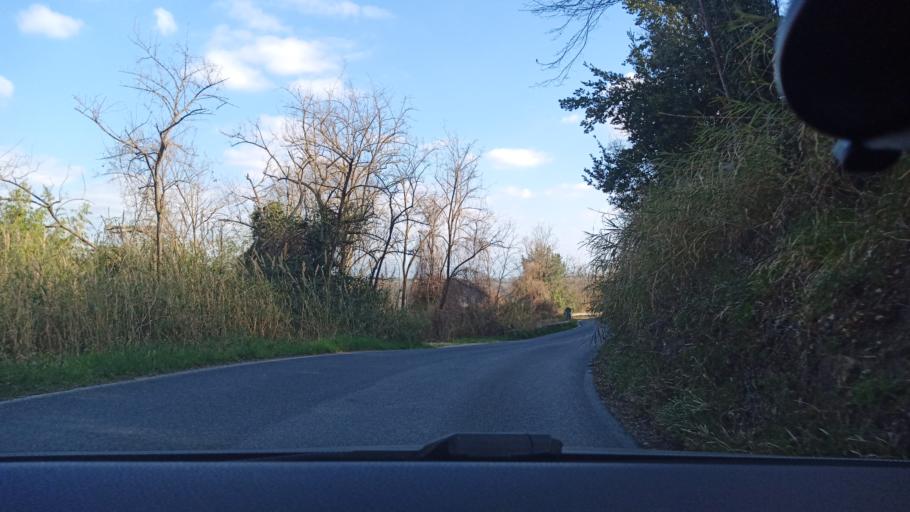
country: IT
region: Latium
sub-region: Citta metropolitana di Roma Capitale
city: Torrita Tiberina
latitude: 42.2477
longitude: 12.6183
